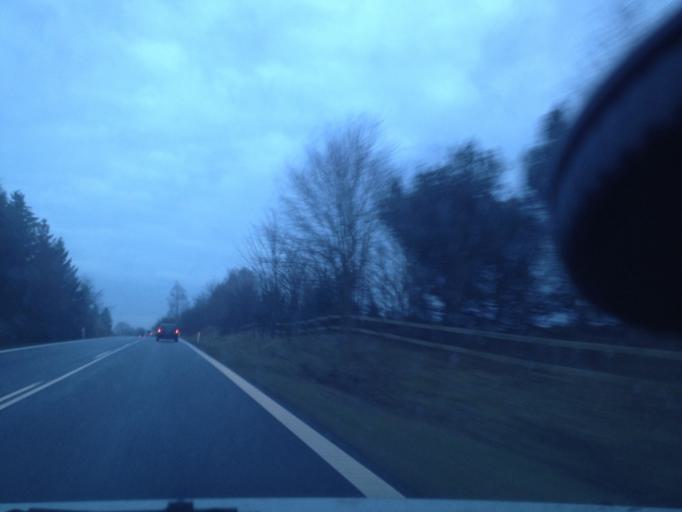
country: DK
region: Capital Region
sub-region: Rudersdal Kommune
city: Birkerod
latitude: 55.8952
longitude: 12.4301
